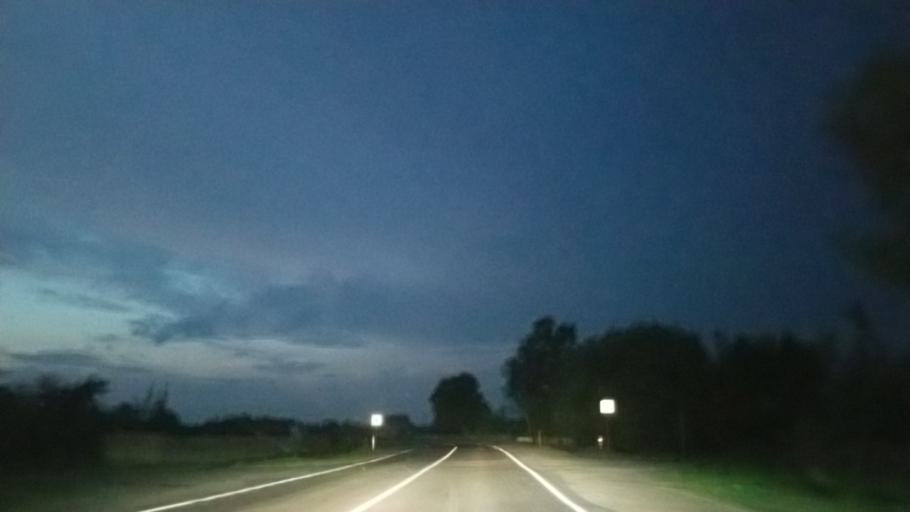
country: PL
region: Lublin Voivodeship
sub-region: Powiat bialski
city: Koden
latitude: 51.9223
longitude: 23.6607
